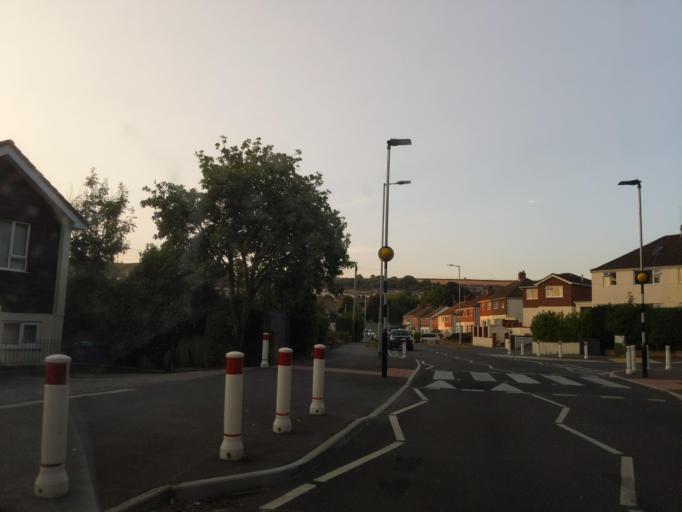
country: GB
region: England
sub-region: Devon
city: Plympton
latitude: 50.3937
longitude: -4.0694
